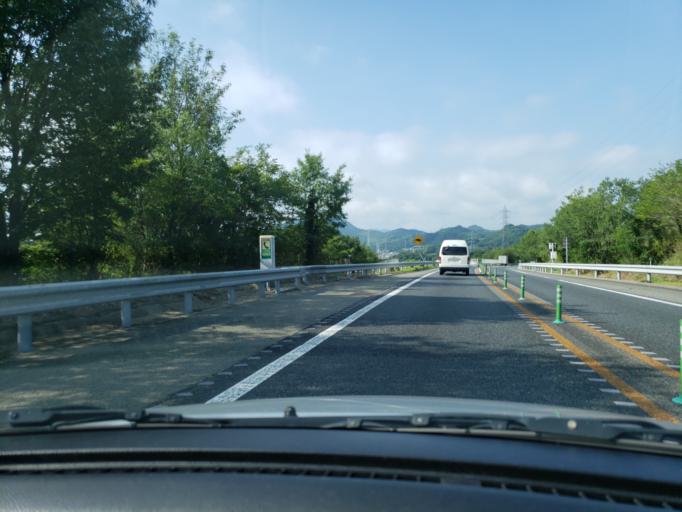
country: JP
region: Hiroshima
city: Onomichi
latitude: 34.4043
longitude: 133.2122
